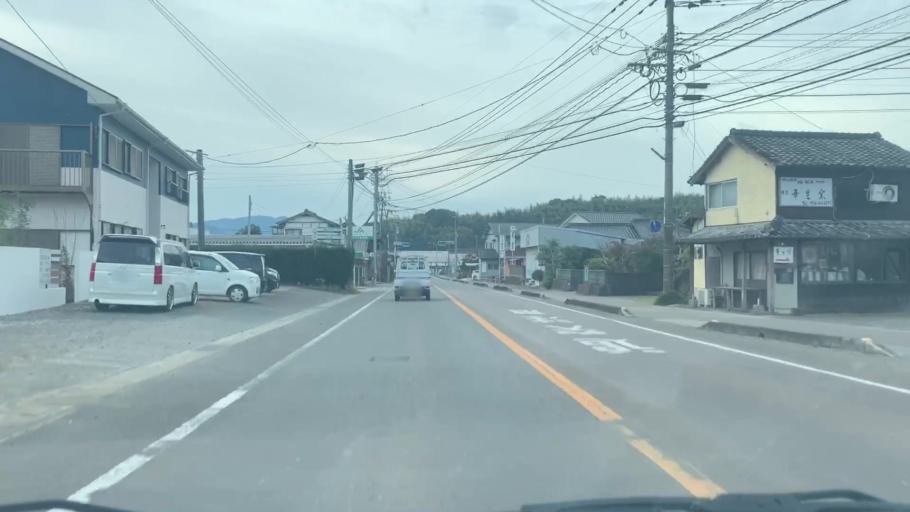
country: JP
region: Saga Prefecture
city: Kashima
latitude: 33.1487
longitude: 130.0631
